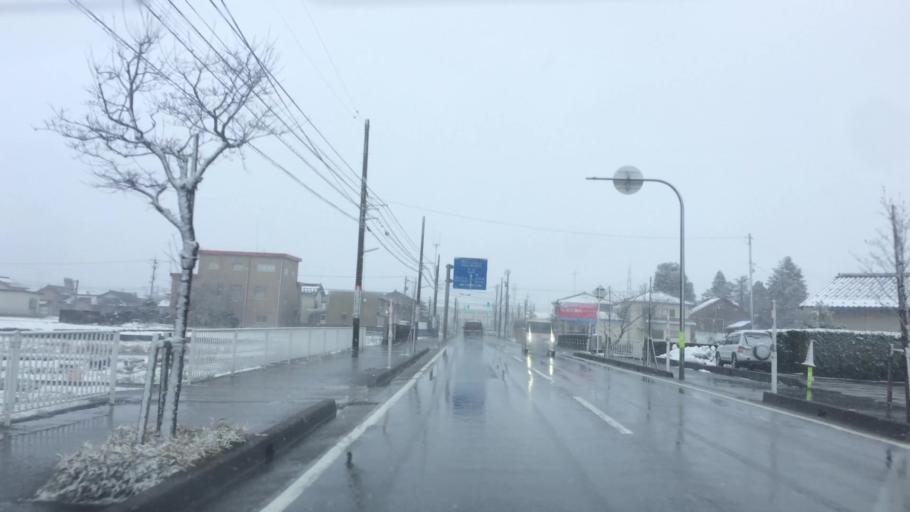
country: JP
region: Toyama
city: Toyama-shi
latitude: 36.6309
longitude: 137.2180
